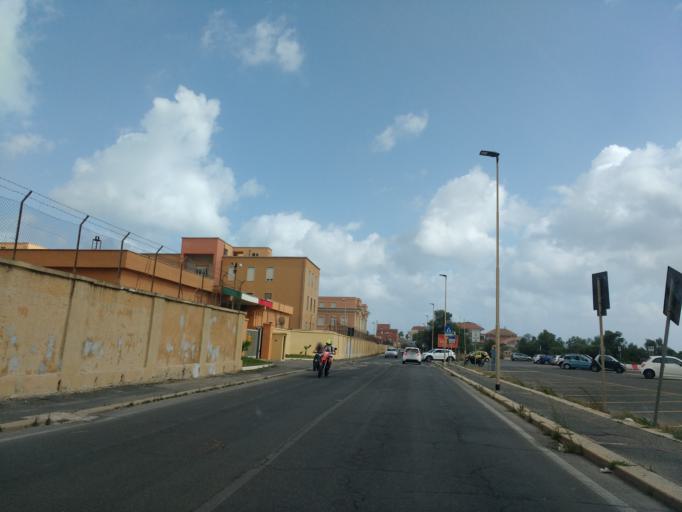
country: IT
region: Latium
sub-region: Citta metropolitana di Roma Capitale
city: Anzio
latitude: 41.4535
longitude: 12.6183
